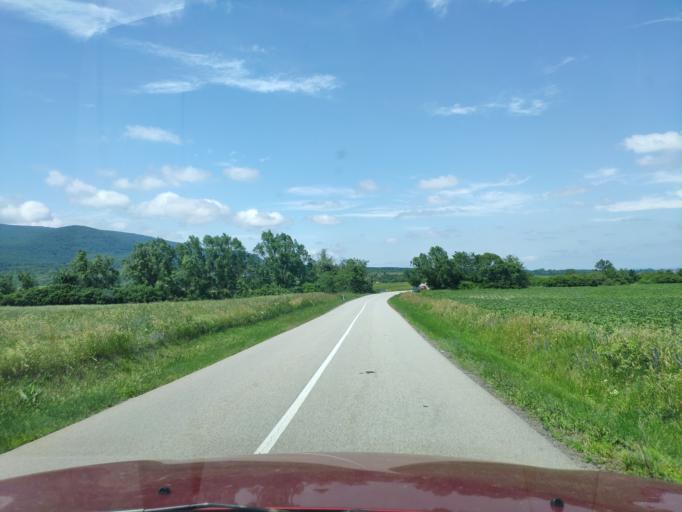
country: SK
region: Kosicky
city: Secovce
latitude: 48.7491
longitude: 21.6439
